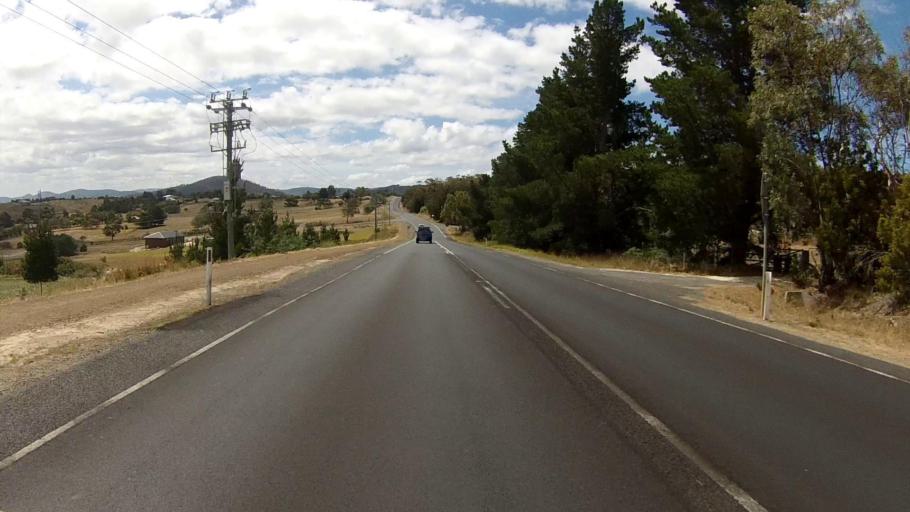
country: AU
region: Tasmania
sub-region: Sorell
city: Sorell
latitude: -42.8237
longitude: 147.6233
